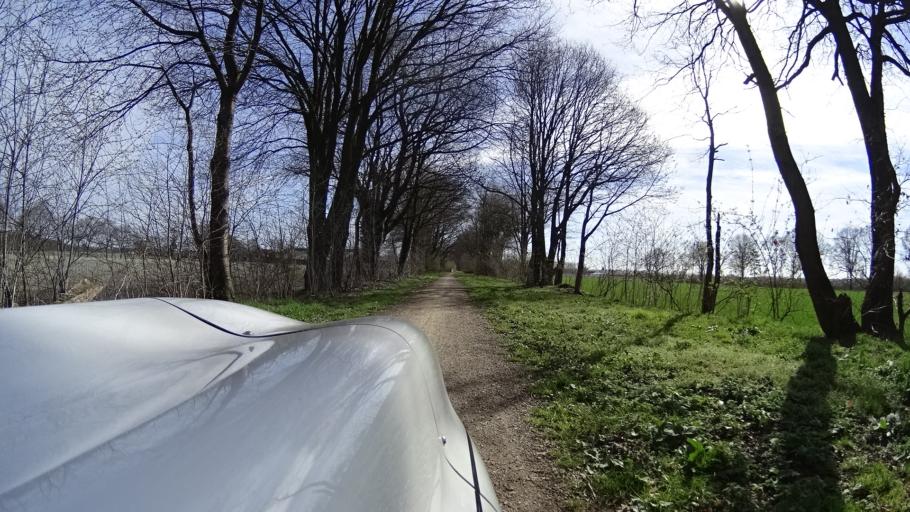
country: NL
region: Limburg
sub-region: Gemeente Gennep
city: Gennep
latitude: 51.6887
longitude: 6.0188
